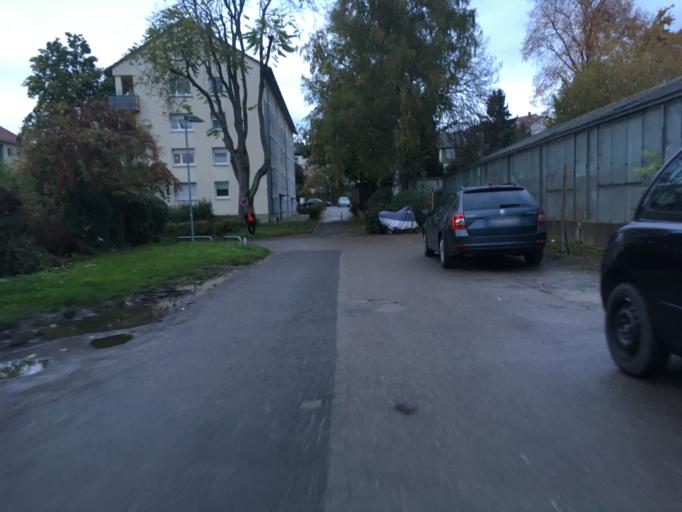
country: DE
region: Baden-Wuerttemberg
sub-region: Regierungsbezirk Stuttgart
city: Heilbronn
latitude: 49.1238
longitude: 9.2159
